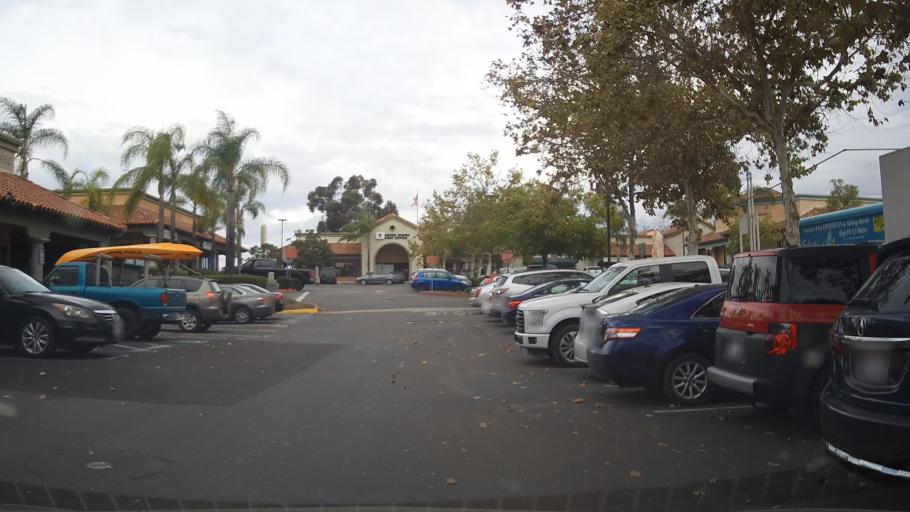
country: US
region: California
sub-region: San Diego County
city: La Mesa
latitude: 32.8395
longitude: -117.0980
